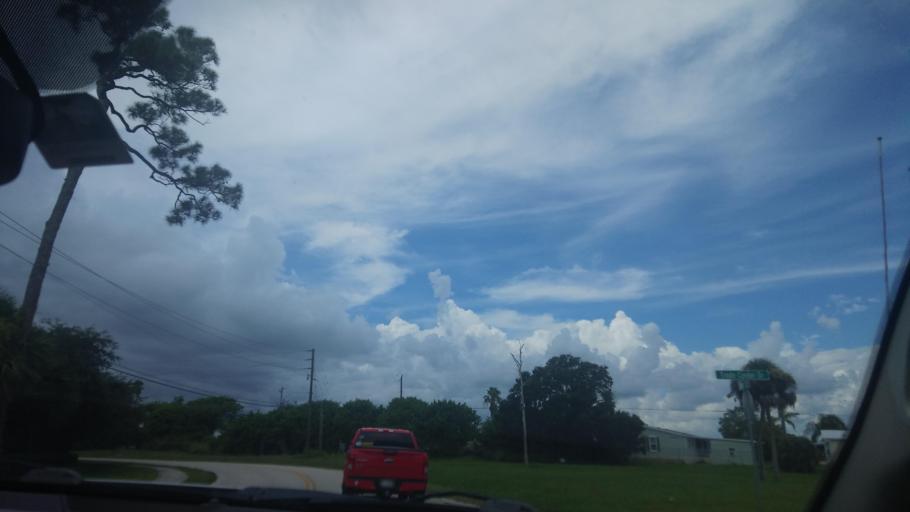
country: US
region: Florida
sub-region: Indian River County
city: Wabasso Beach
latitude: 27.7682
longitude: -80.4488
